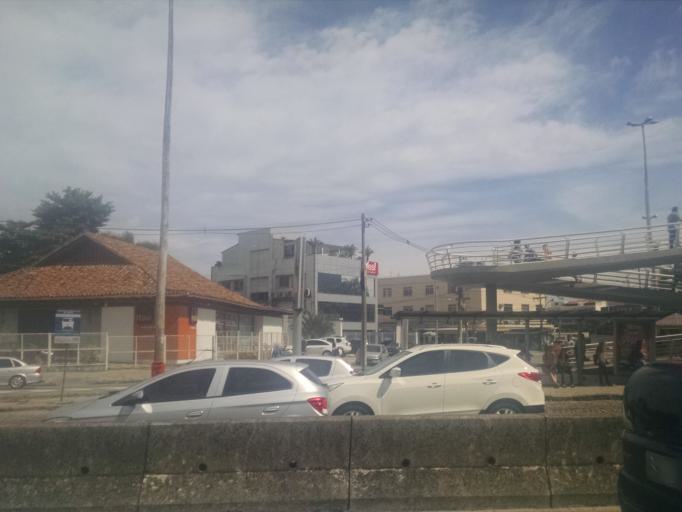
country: BR
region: Rio de Janeiro
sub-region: Rio De Janeiro
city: Rio de Janeiro
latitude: -23.0085
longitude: -43.3035
